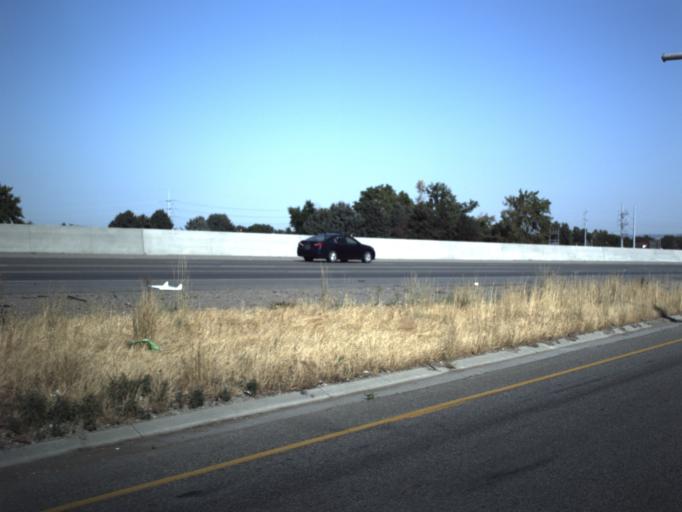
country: US
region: Utah
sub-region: Davis County
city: West Bountiful
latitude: 40.8861
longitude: -111.8961
